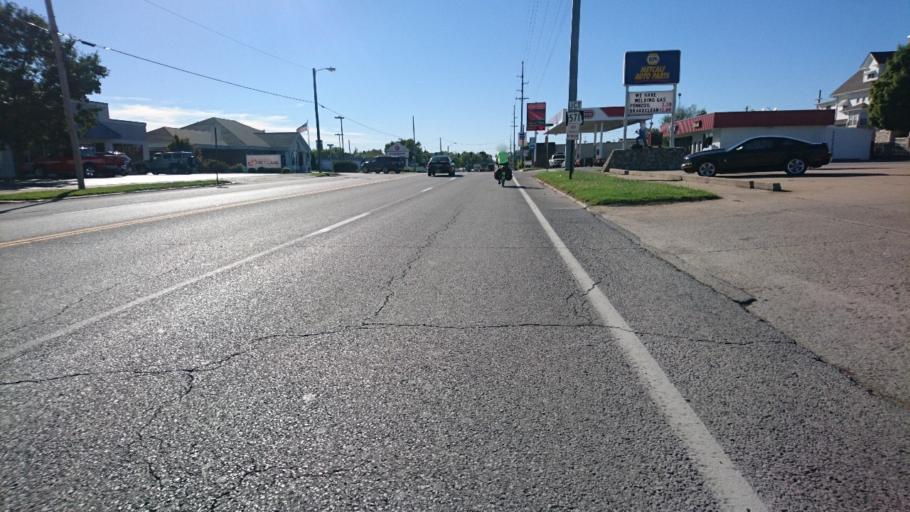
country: US
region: Missouri
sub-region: Jasper County
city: Carthage
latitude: 37.1787
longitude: -94.3118
